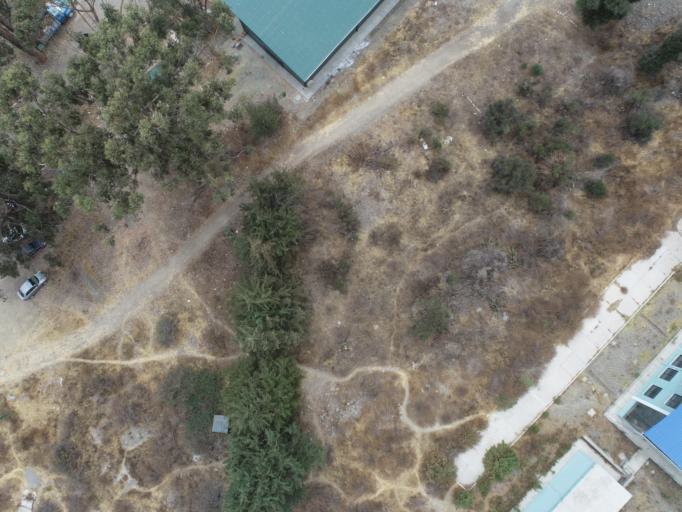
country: BO
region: La Paz
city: La Paz
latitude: -16.5390
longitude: -68.0622
